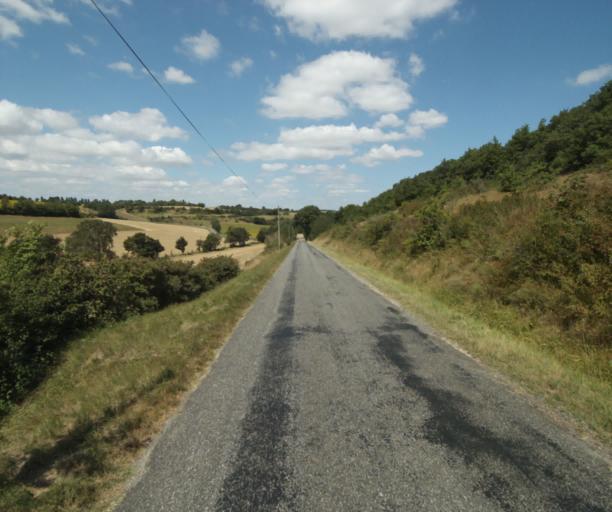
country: FR
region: Midi-Pyrenees
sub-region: Departement de la Haute-Garonne
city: Saint-Felix-Lauragais
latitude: 43.4678
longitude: 1.8521
